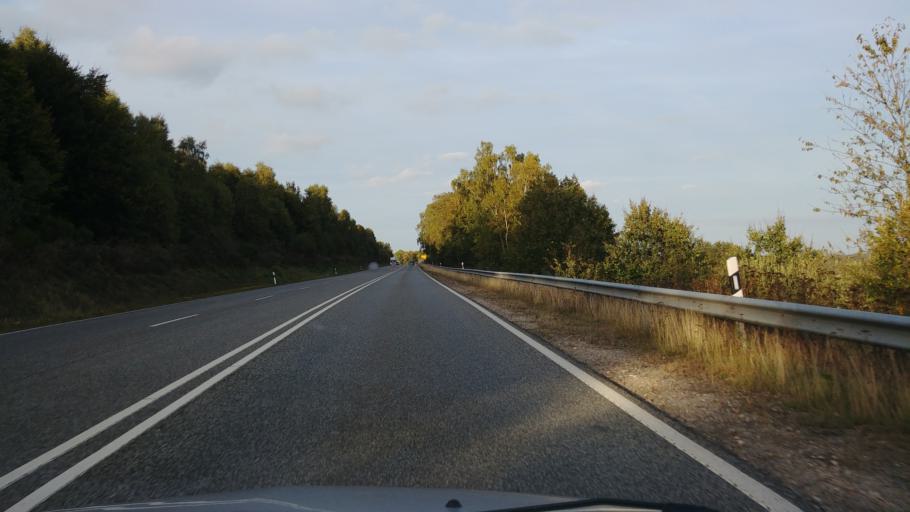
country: DE
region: Rheinland-Pfalz
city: Kommen
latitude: 49.8485
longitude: 7.1585
